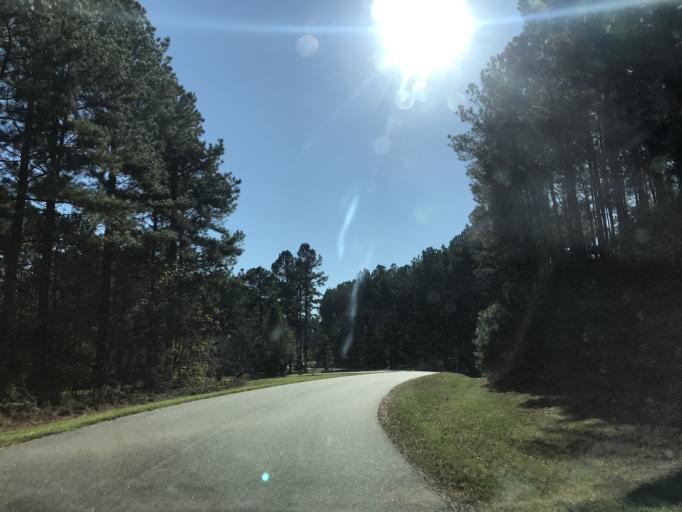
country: US
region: North Carolina
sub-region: Wake County
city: Rolesville
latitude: 35.9631
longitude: -78.3678
